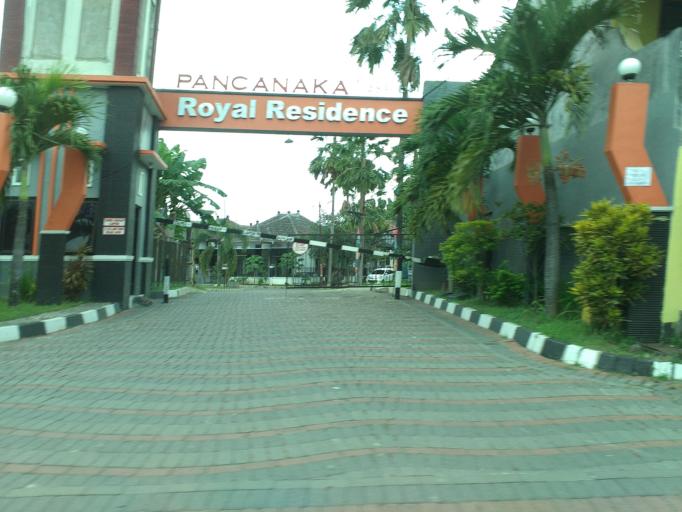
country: ID
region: Central Java
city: Ceper
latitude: -7.6591
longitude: 110.6756
